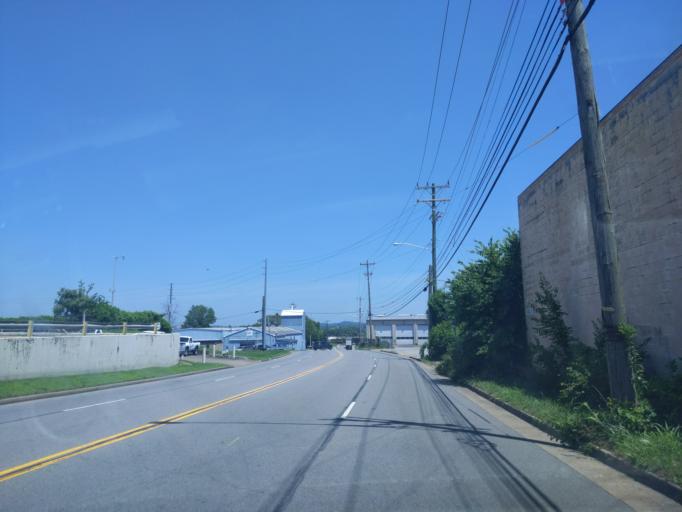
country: US
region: Tennessee
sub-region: Davidson County
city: Nashville
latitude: 36.1359
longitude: -86.7467
